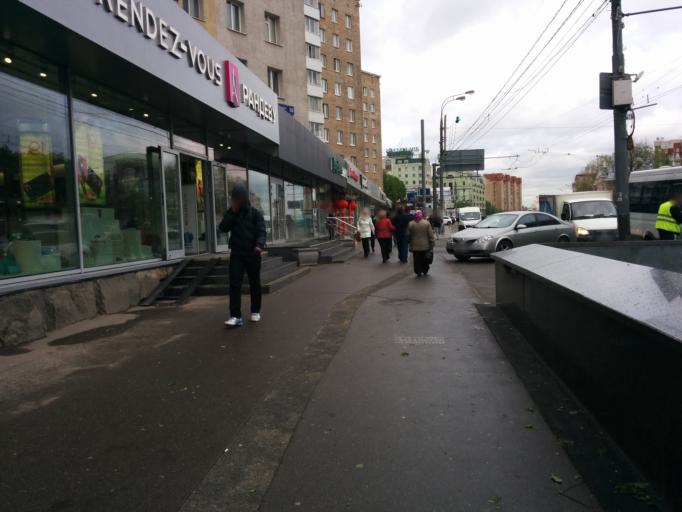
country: RU
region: Moscow
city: Moscow
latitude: 55.7308
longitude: 37.6117
